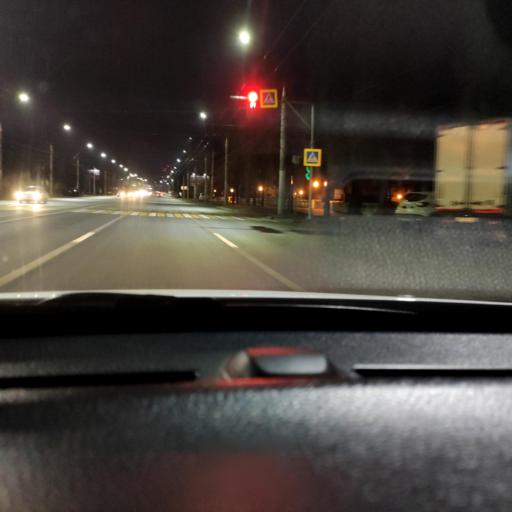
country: RU
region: Voronezj
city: Voronezh
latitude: 51.6823
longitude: 39.2617
